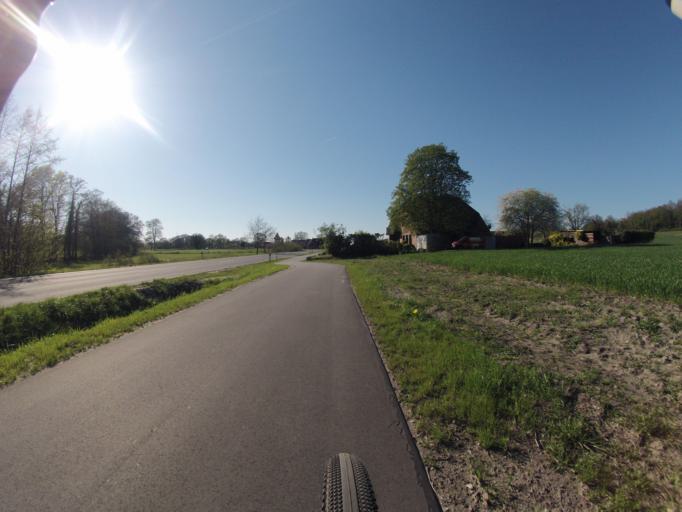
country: DE
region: North Rhine-Westphalia
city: Ibbenburen
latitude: 52.2324
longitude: 7.7058
